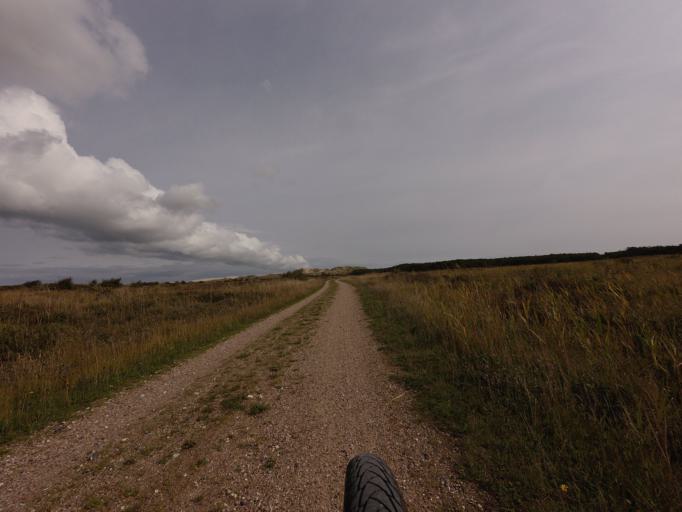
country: DK
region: North Denmark
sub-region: Frederikshavn Kommune
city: Strandby
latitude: 57.6406
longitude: 10.4013
